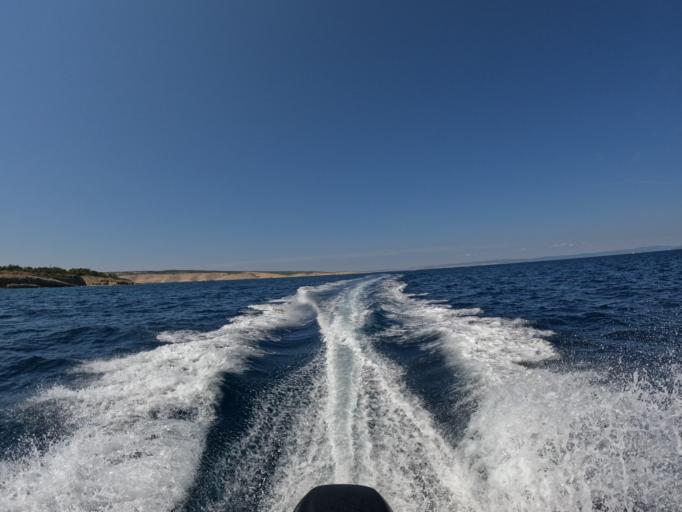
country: HR
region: Primorsko-Goranska
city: Lopar
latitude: 44.8546
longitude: 14.7235
